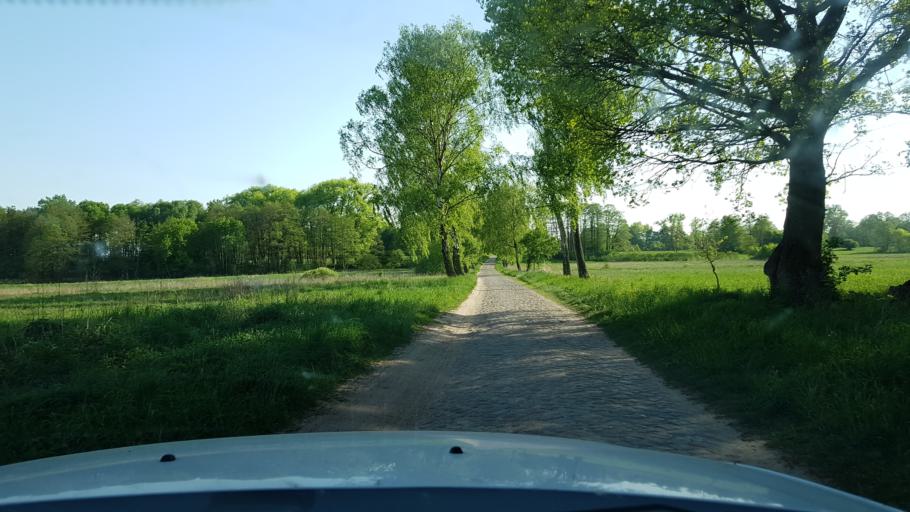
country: PL
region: West Pomeranian Voivodeship
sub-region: Powiat lobeski
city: Resko
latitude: 53.7144
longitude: 15.3381
